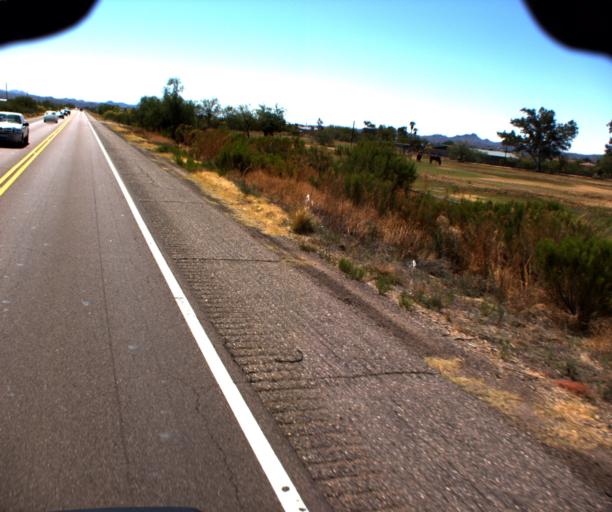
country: US
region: Arizona
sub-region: Maricopa County
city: Wickenburg
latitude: 34.0104
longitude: -112.7868
